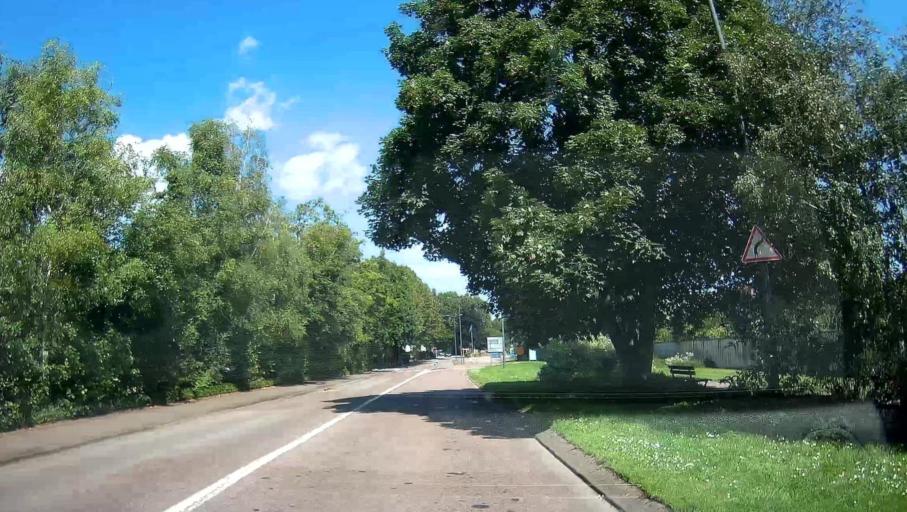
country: FR
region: Bourgogne
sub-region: Departement de la Cote-d'Or
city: Beaune
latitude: 47.0189
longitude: 4.8356
